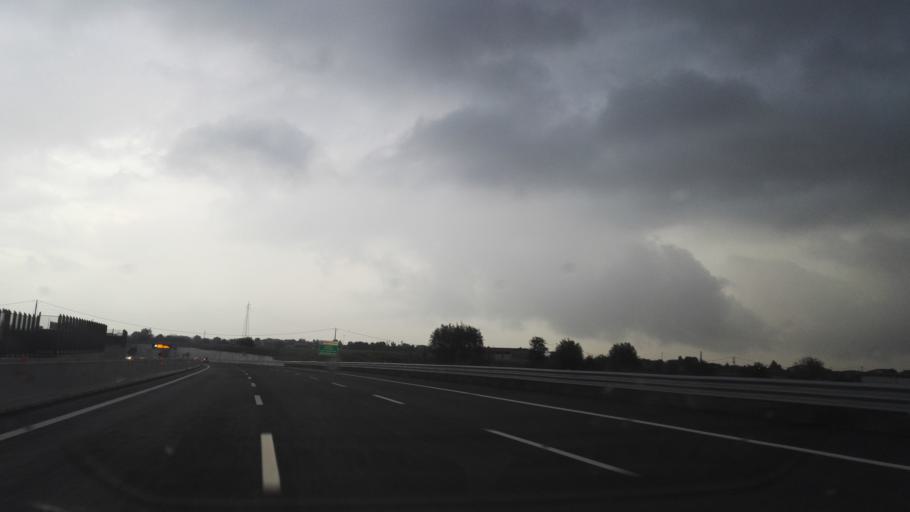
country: IT
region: Lombardy
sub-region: Citta metropolitana di Milano
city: Bellinzago Lombardo
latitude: 45.5339
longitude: 9.4385
